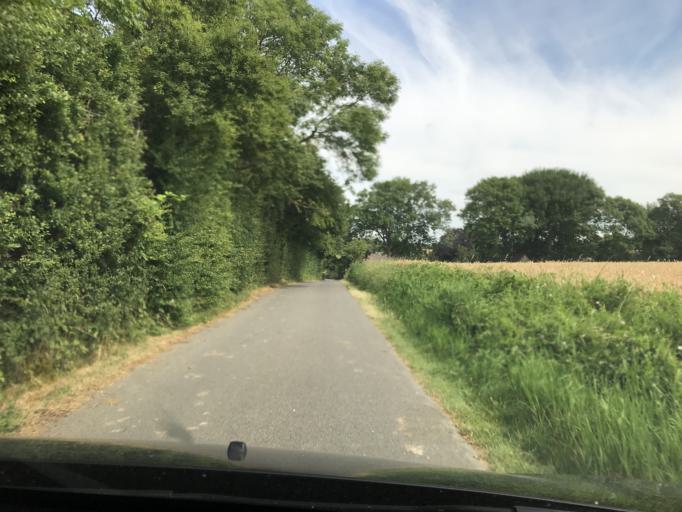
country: DK
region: South Denmark
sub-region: AEro Kommune
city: AEroskobing
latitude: 54.9115
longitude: 10.2798
